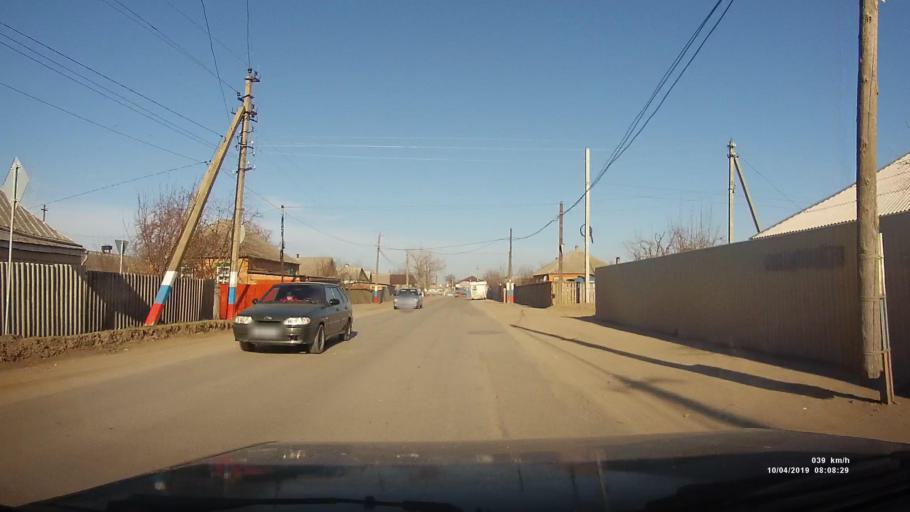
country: RU
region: Rostov
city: Staraya Stanitsa
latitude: 48.3482
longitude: 40.2849
